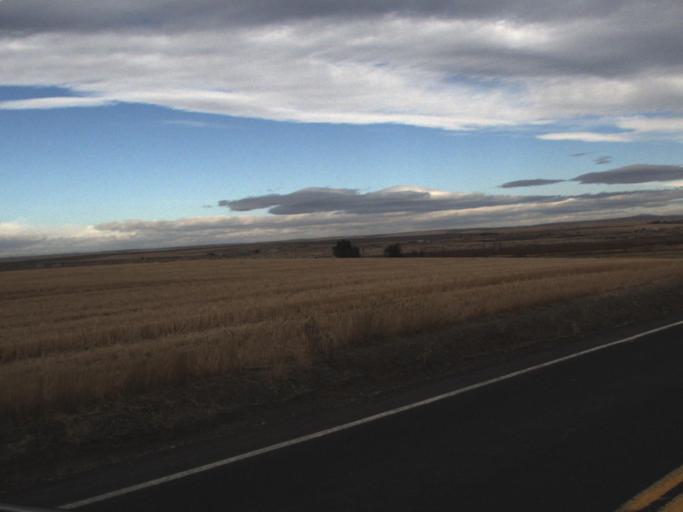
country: US
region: Washington
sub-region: Okanogan County
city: Coulee Dam
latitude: 47.7388
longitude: -118.7218
